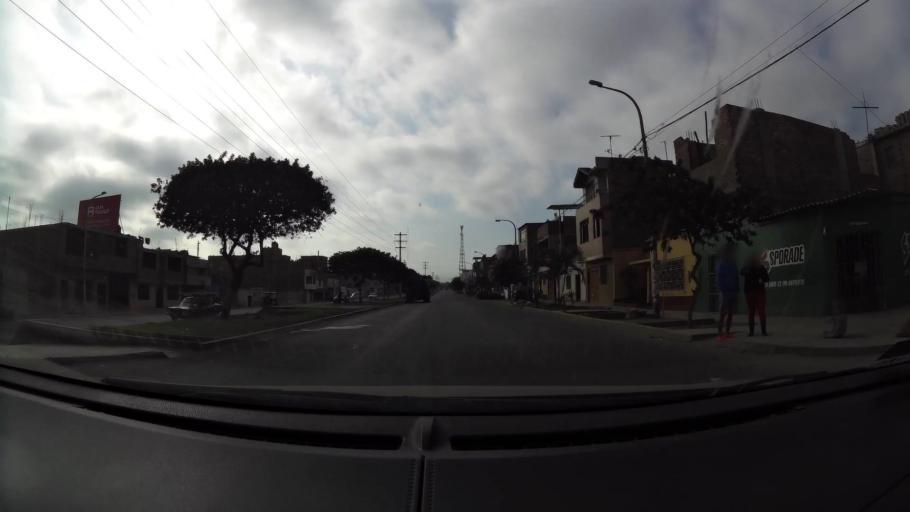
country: PE
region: La Libertad
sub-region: Provincia de Trujillo
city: La Esperanza
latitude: -8.0765
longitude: -79.0465
